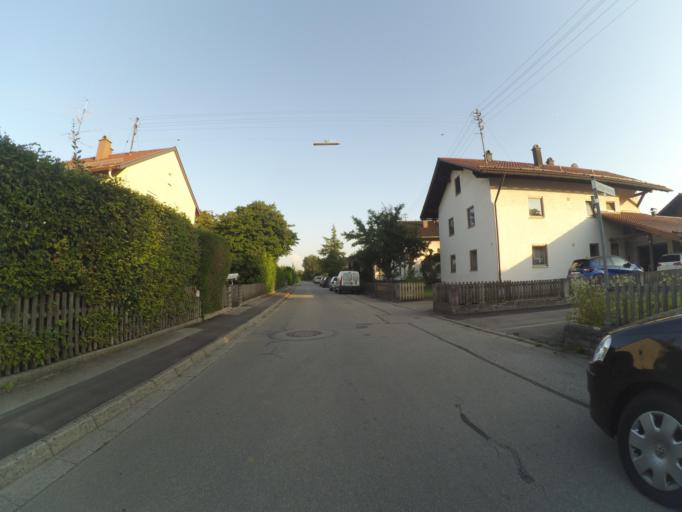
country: DE
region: Bavaria
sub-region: Swabia
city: Jengen
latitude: 47.9977
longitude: 10.7255
